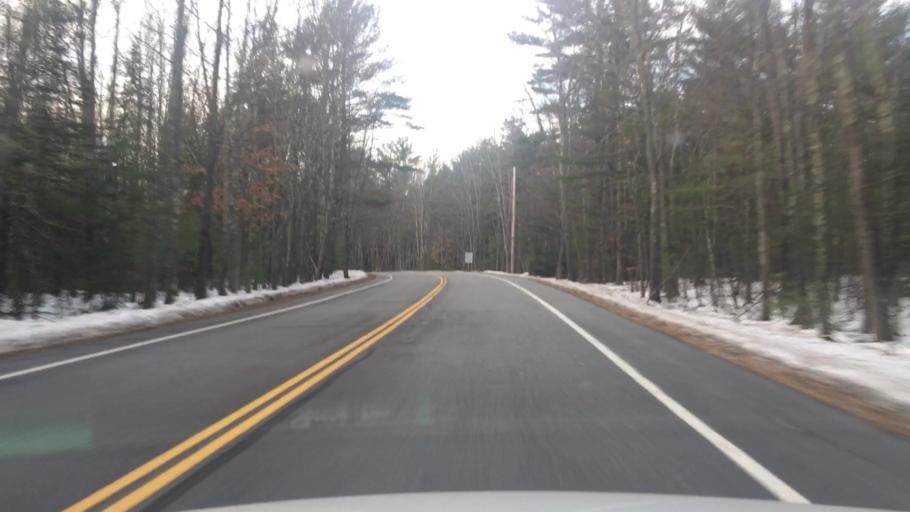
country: US
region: Maine
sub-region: York County
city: Dayton
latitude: 43.5647
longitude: -70.6222
